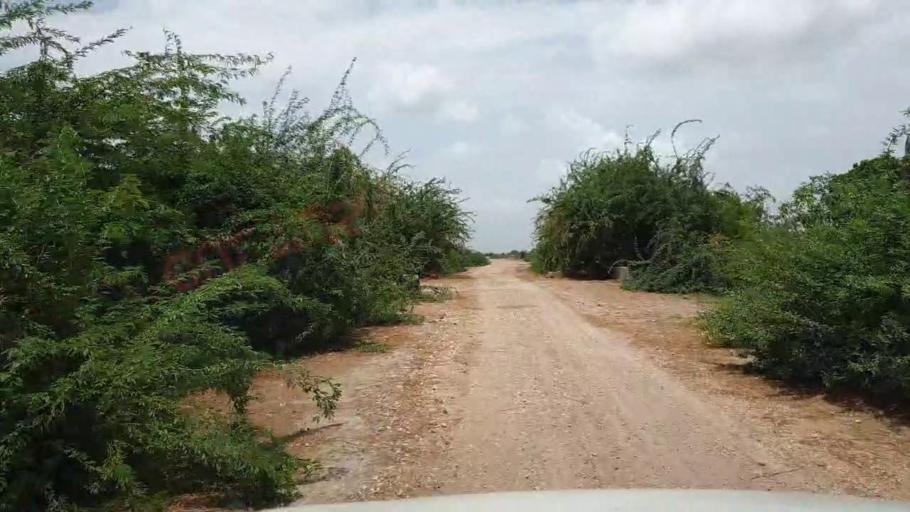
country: PK
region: Sindh
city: Kario
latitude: 24.7187
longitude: 68.5769
